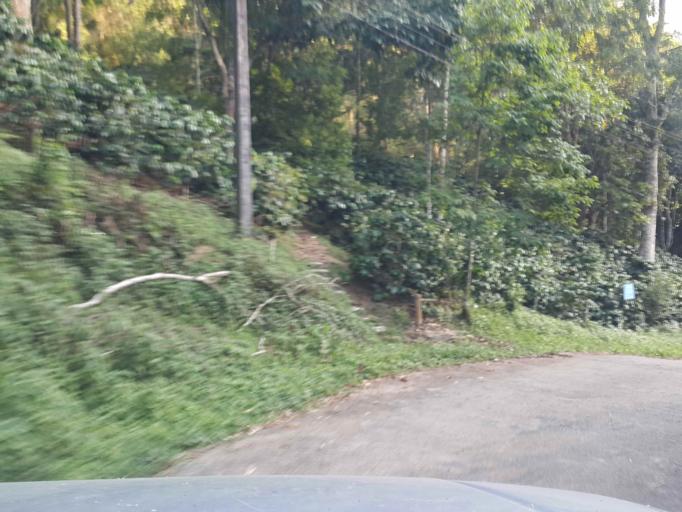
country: TH
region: Chiang Mai
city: Mae On
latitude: 18.9247
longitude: 99.3568
